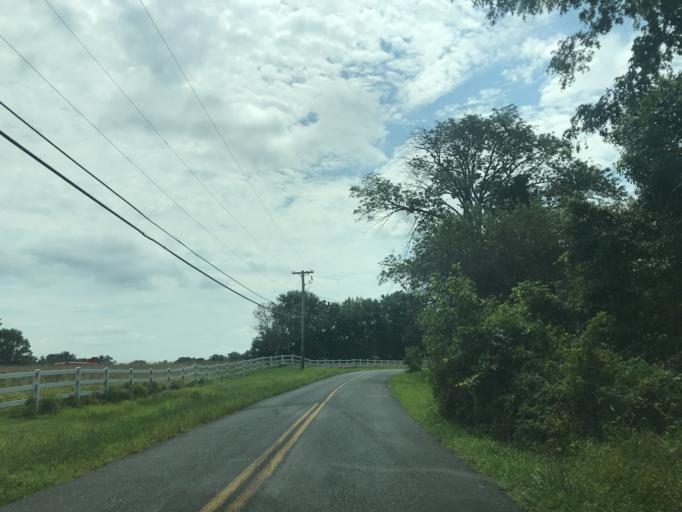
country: US
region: Maryland
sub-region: Harford County
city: Fallston
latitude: 39.5042
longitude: -76.4111
